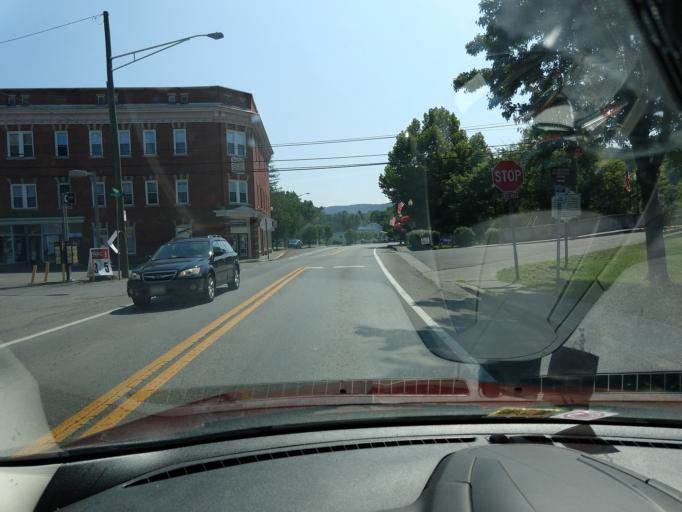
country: US
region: West Virginia
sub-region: Greenbrier County
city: Alderson
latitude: 37.7255
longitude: -80.6407
